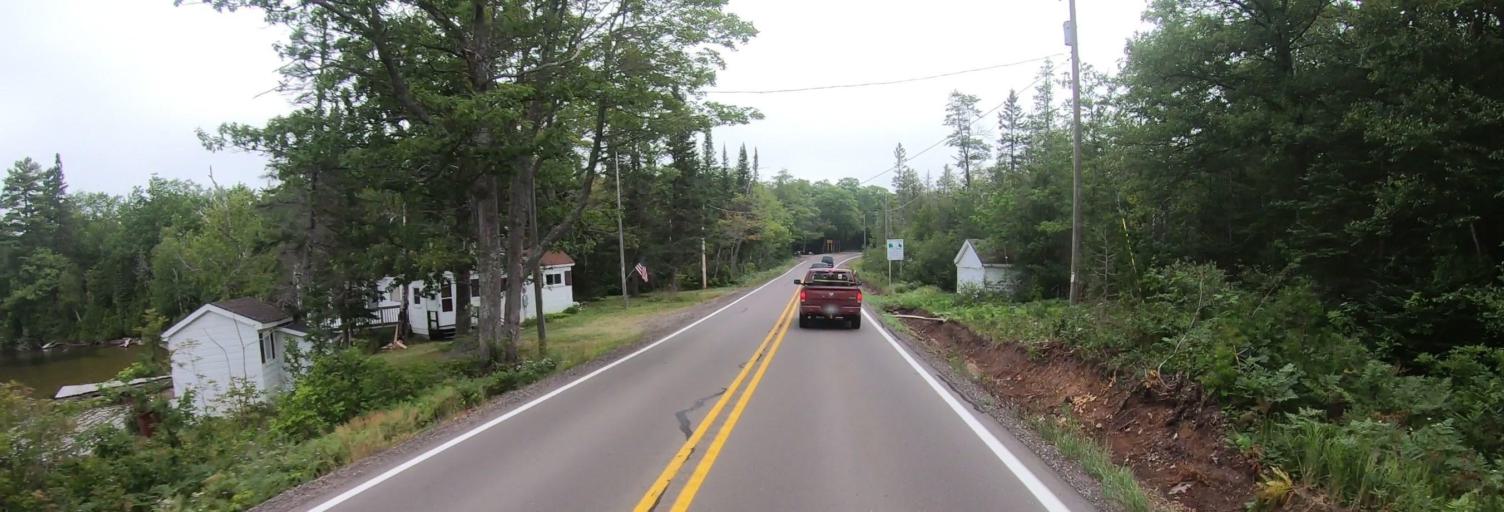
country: US
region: Michigan
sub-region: Keweenaw County
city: Eagle River
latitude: 47.4372
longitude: -87.9601
